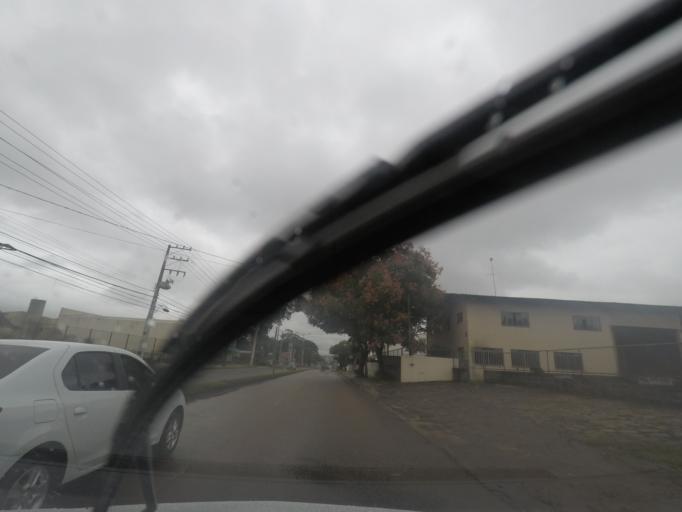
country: BR
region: Parana
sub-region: Pinhais
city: Pinhais
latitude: -25.3919
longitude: -49.1857
